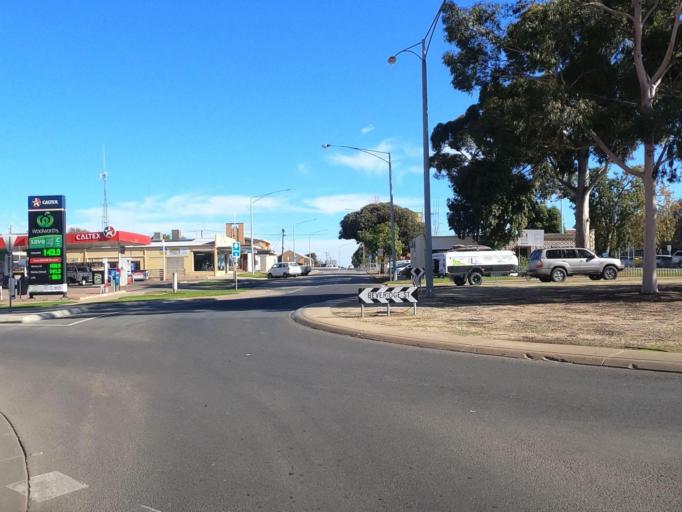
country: AU
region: Victoria
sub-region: Swan Hill
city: Swan Hill
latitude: -35.3390
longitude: 143.5583
